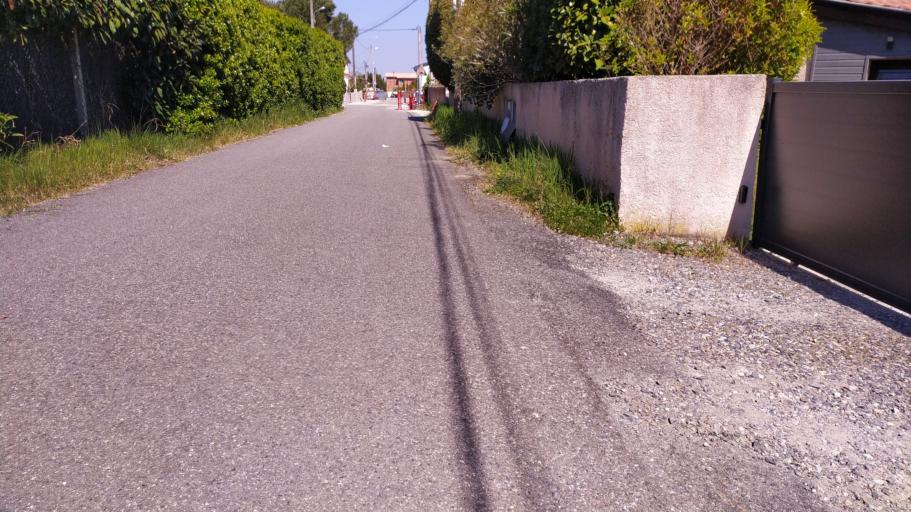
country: FR
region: Midi-Pyrenees
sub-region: Departement de la Haute-Garonne
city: Tournefeuille
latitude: 43.5845
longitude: 1.3171
